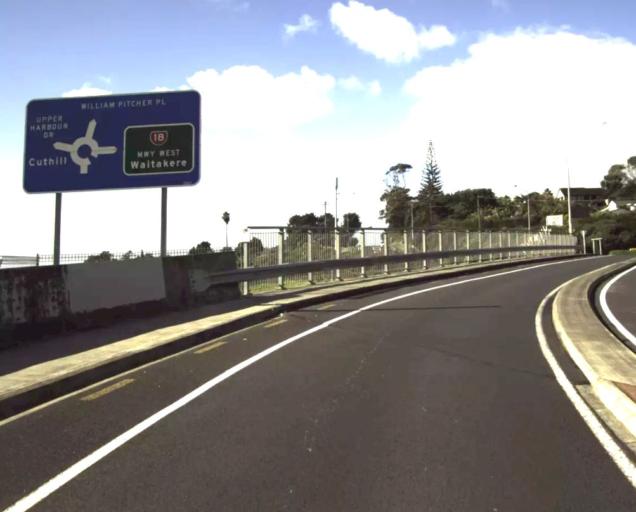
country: NZ
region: Auckland
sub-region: Auckland
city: North Shore
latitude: -36.7812
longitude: 174.6771
